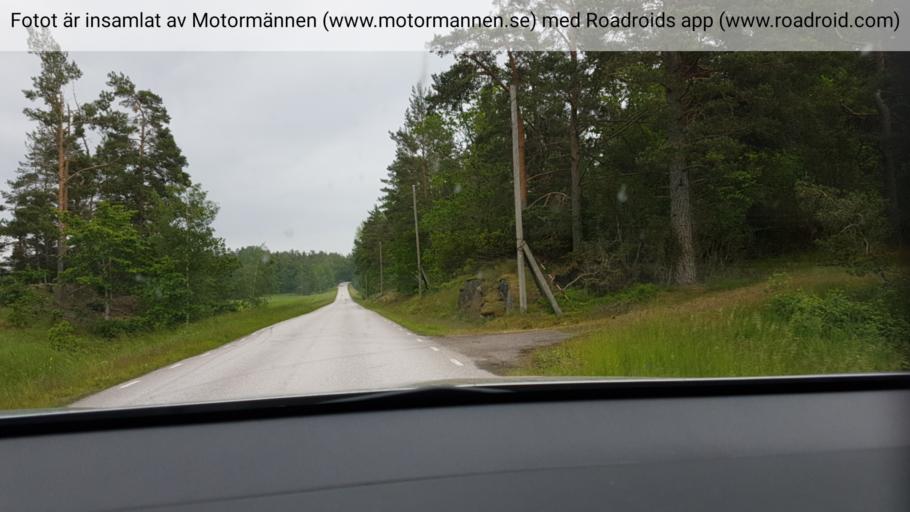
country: SE
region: OEstergoetland
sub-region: Valdemarsviks Kommun
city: Valdemarsvik
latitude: 58.1213
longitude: 16.6414
